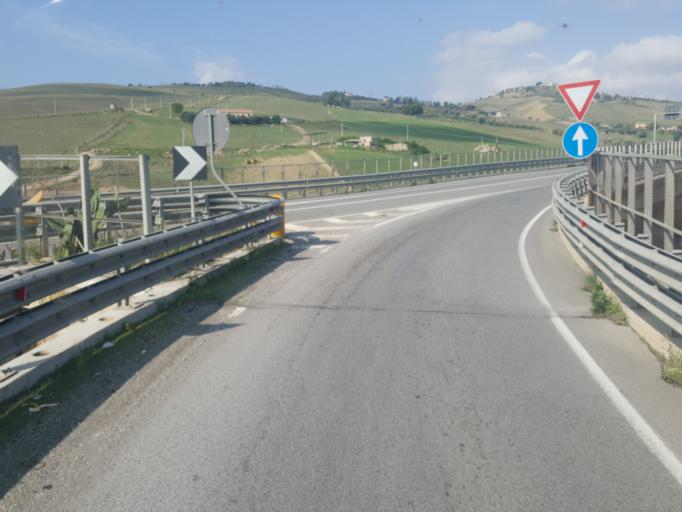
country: IT
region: Sicily
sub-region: Enna
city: Pietraperzia
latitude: 37.4578
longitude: 14.1070
